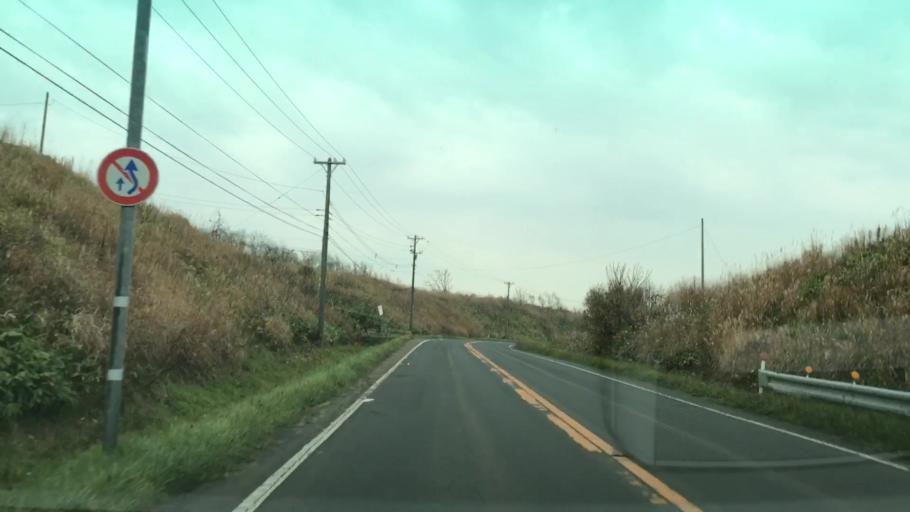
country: JP
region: Hokkaido
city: Ishikari
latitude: 43.3862
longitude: 141.4328
